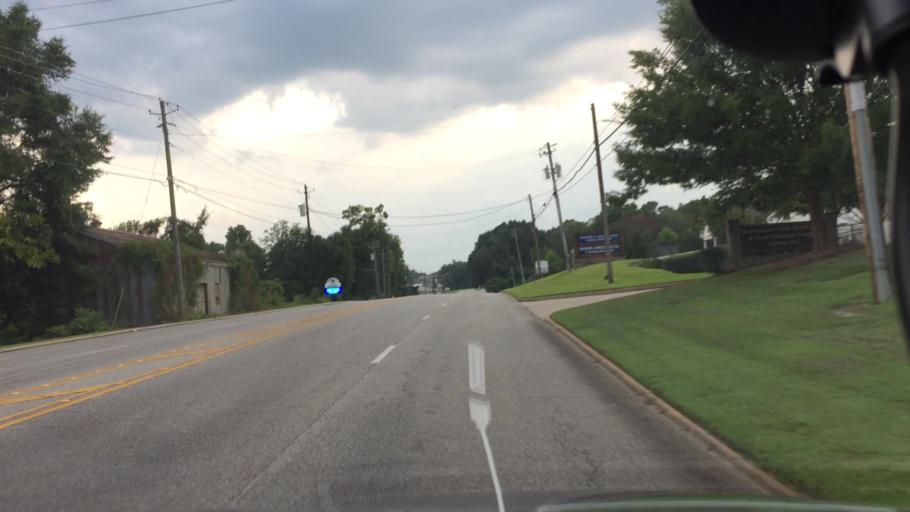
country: US
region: Alabama
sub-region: Coffee County
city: Enterprise
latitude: 31.3266
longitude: -85.8411
